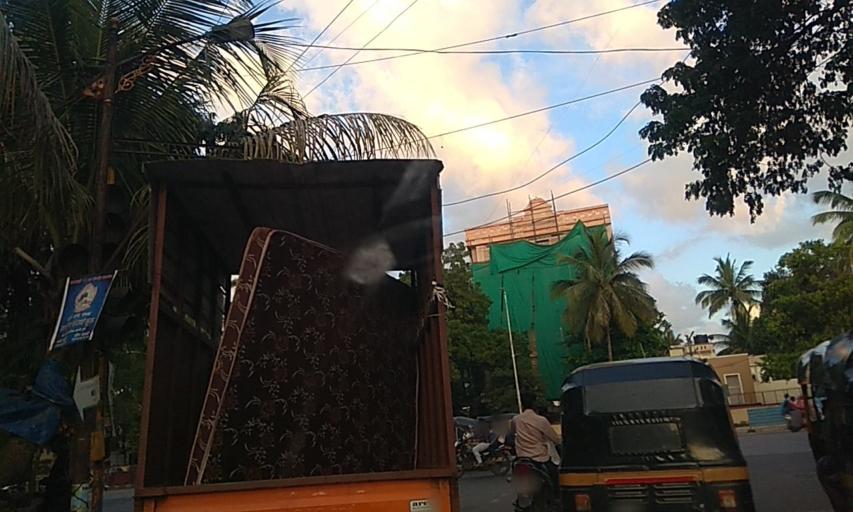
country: IN
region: Maharashtra
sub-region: Pune Division
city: Pune
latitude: 18.4925
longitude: 73.8575
